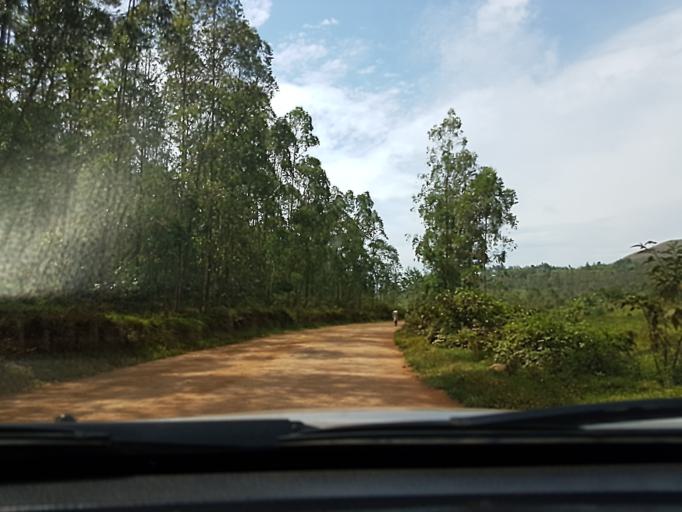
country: CD
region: South Kivu
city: Bukavu
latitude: -2.6489
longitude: 28.8738
